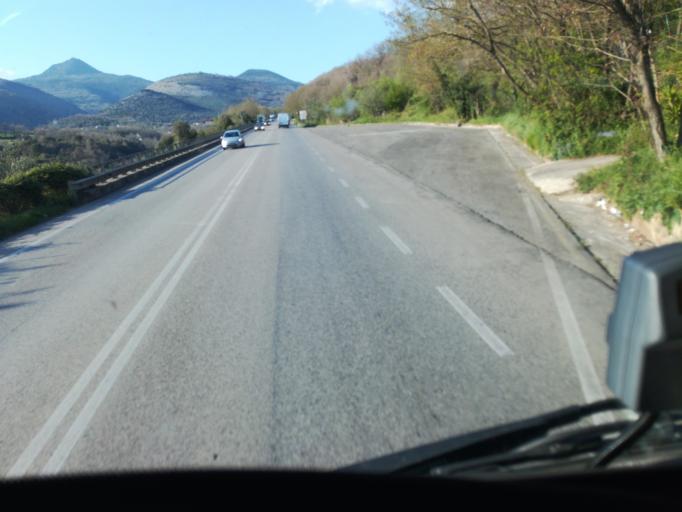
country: IT
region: Latium
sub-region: Provincia di Latina
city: Prossedi
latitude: 41.5271
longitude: 13.2684
